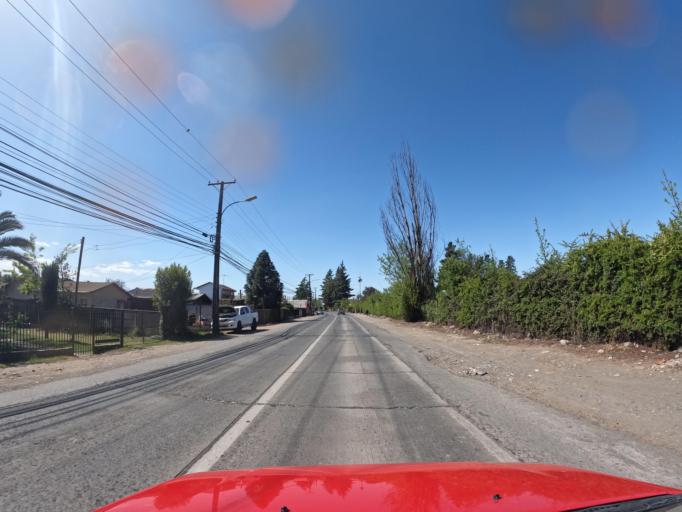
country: CL
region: Maule
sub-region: Provincia de Curico
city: Molina
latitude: -35.0764
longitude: -71.2589
